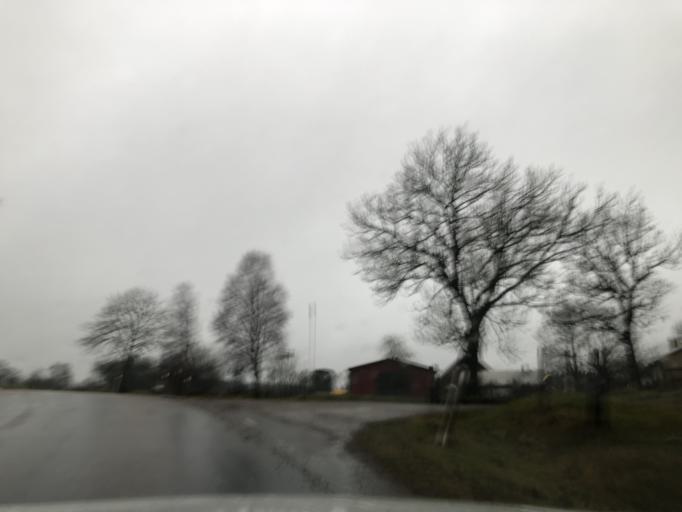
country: SE
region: Vaestra Goetaland
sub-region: Ulricehamns Kommun
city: Ulricehamn
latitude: 57.8486
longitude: 13.5423
